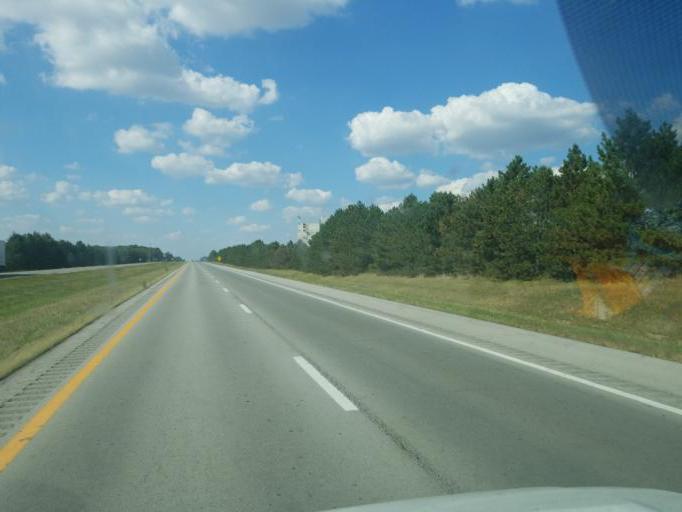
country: US
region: Ohio
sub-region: Wyandot County
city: Upper Sandusky
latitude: 40.8717
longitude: -83.3283
